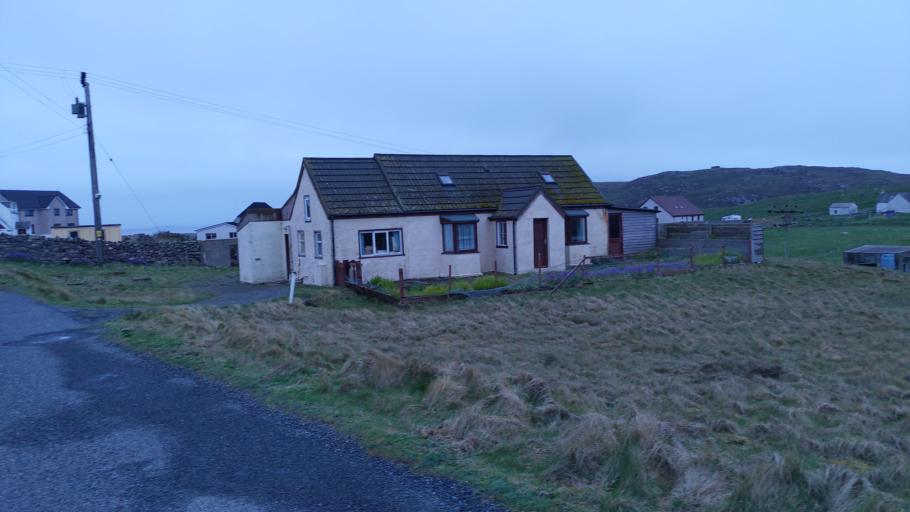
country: GB
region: Scotland
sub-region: Shetland Islands
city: Shetland
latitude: 60.4228
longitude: -0.7654
